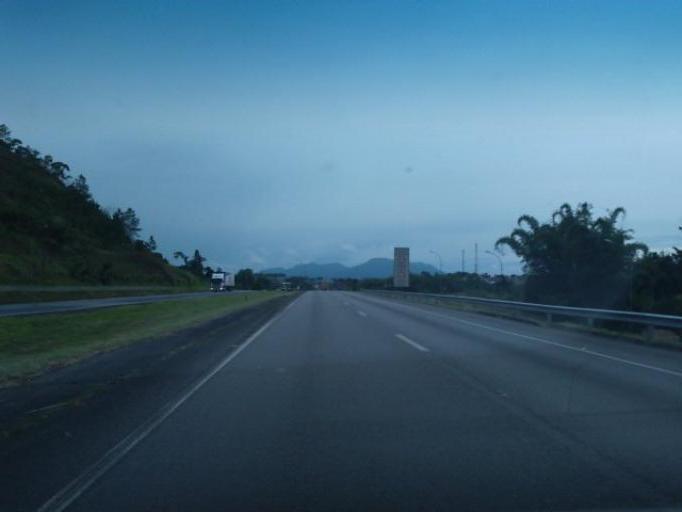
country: BR
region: Sao Paulo
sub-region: Jacupiranga
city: Jacupiranga
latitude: -24.6904
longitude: -47.9935
